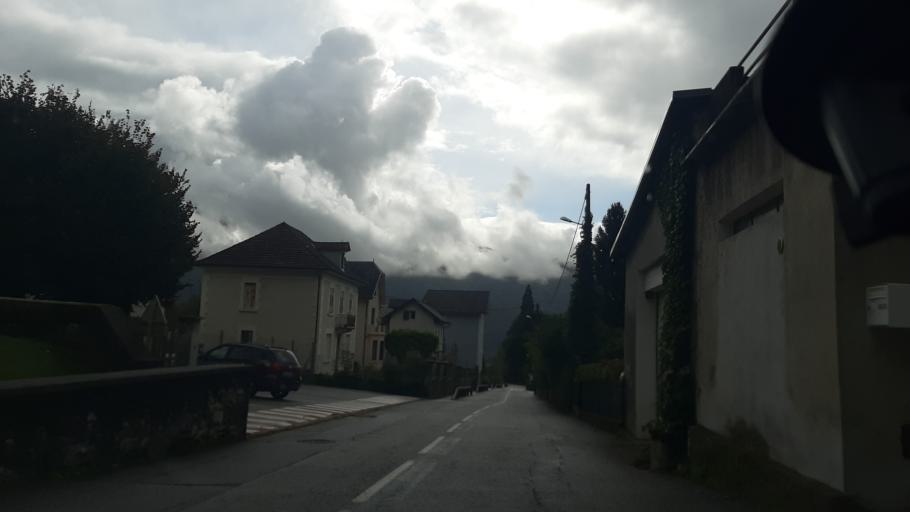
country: FR
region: Rhone-Alpes
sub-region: Departement de la Savoie
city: Gresy-sur-Isere
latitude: 45.6007
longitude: 6.2556
